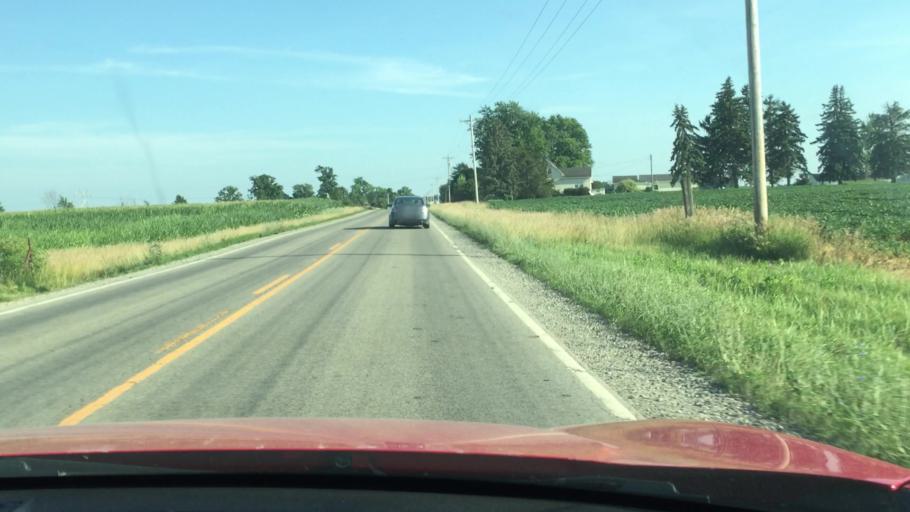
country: US
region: Ohio
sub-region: Hardin County
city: Ada
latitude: 40.6718
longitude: -83.8554
